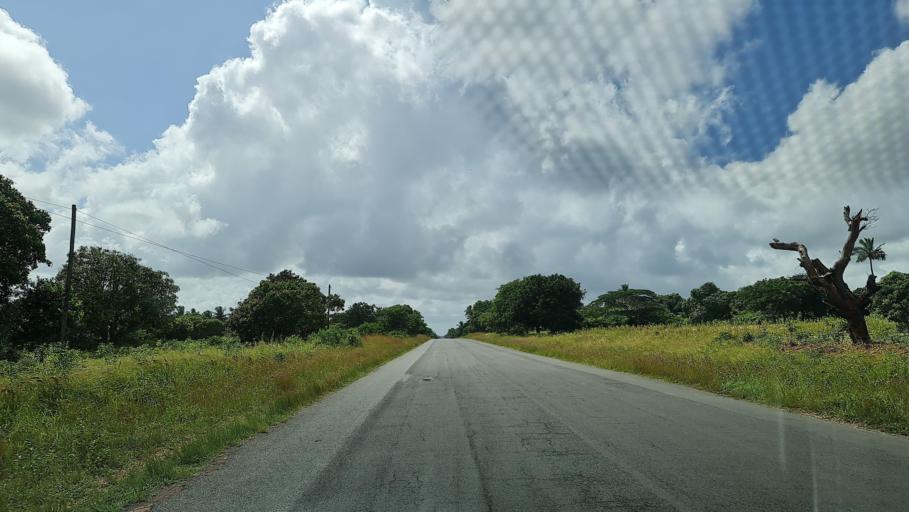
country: MZ
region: Gaza
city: Manjacaze
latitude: -24.6792
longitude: 34.5991
